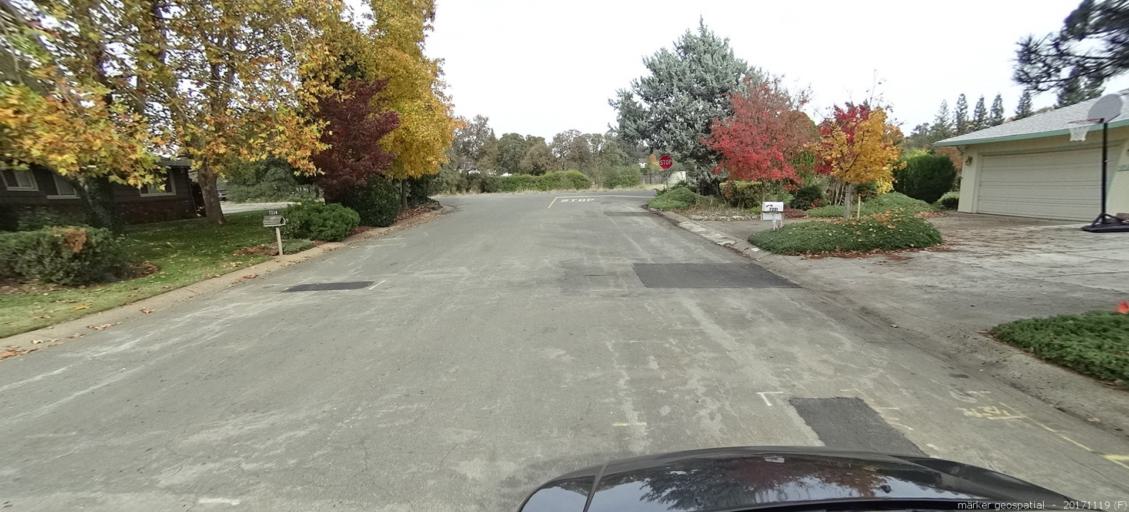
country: US
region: California
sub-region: Shasta County
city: Anderson
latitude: 40.4980
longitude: -122.3080
